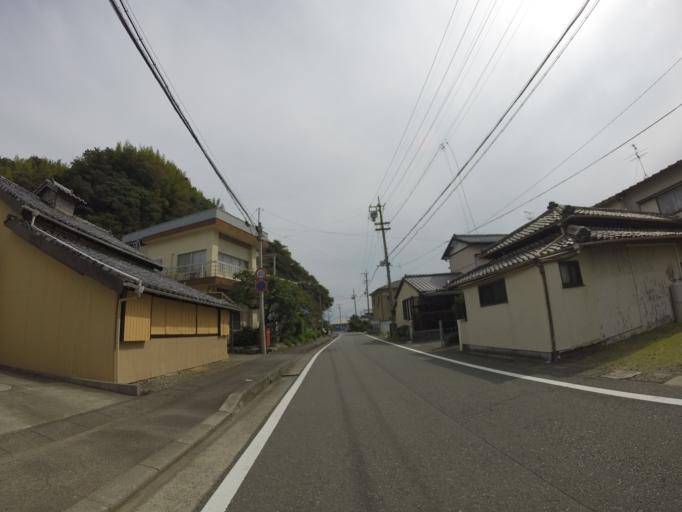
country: JP
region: Shizuoka
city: Shizuoka-shi
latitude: 35.0621
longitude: 138.5320
